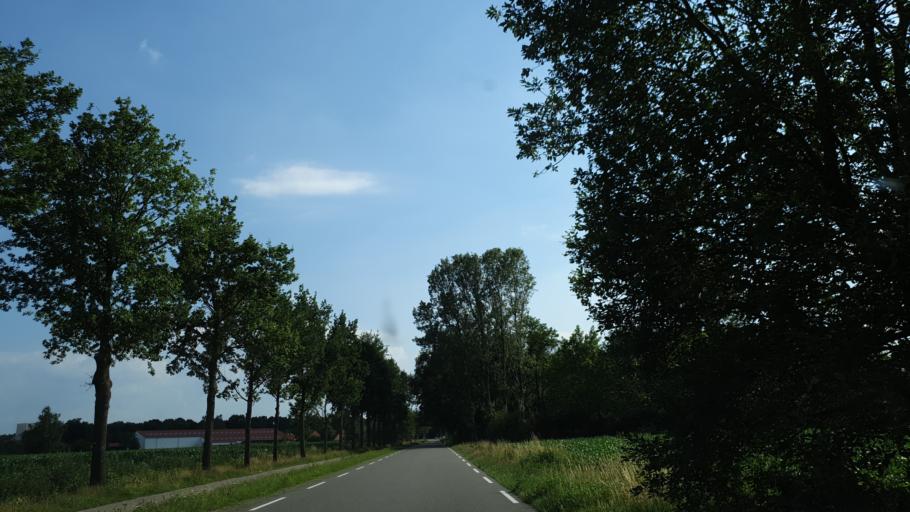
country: NL
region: Limburg
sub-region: Gemeente Weert
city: Weert
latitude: 51.2547
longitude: 5.6540
